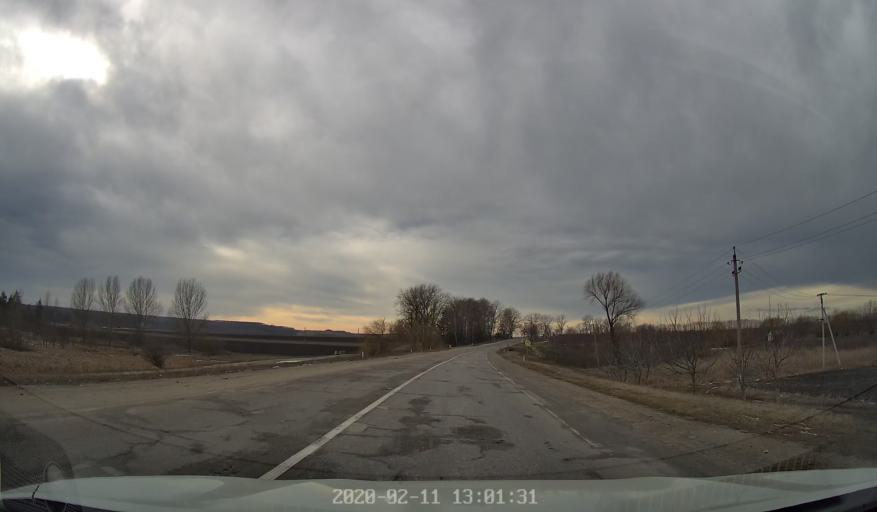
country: MD
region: Briceni
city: Briceni
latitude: 48.3174
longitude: 27.0004
